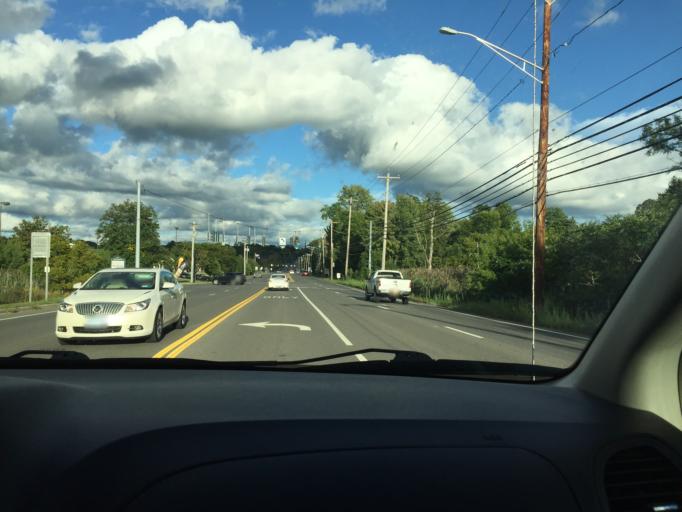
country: US
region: New York
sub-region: Onondaga County
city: Fayetteville
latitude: 43.0290
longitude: -76.0225
